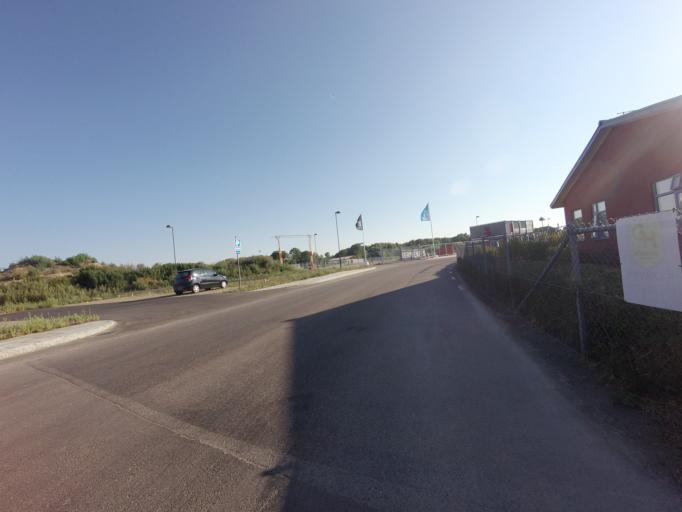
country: SE
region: Skane
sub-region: Landskrona
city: Landskrona
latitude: 55.8971
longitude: 12.8235
